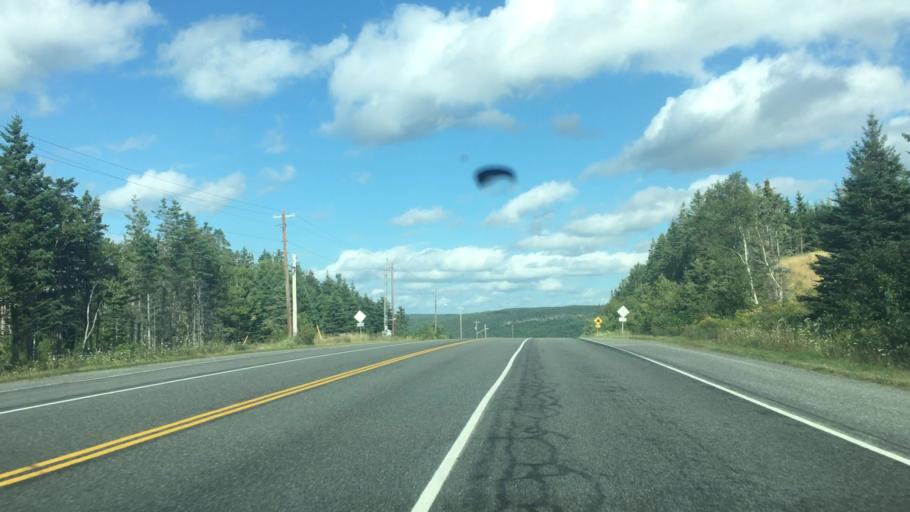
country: CA
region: Nova Scotia
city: Sydney
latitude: 45.8145
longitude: -60.6944
